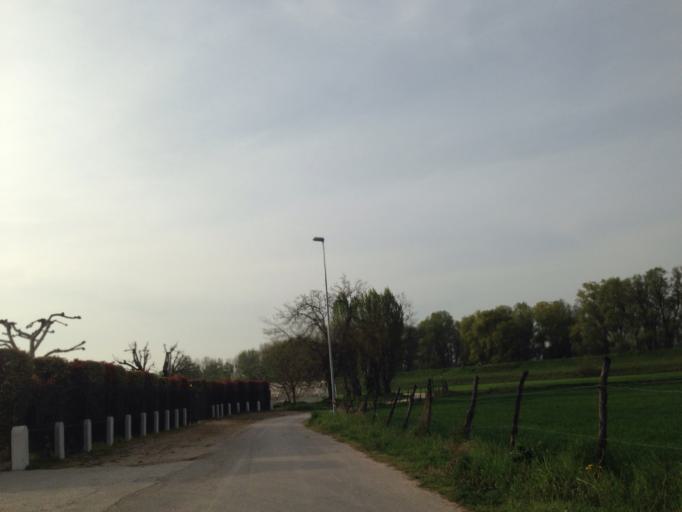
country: IT
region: Veneto
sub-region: Provincia di Verona
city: Zevio
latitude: 45.3758
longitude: 11.1204
